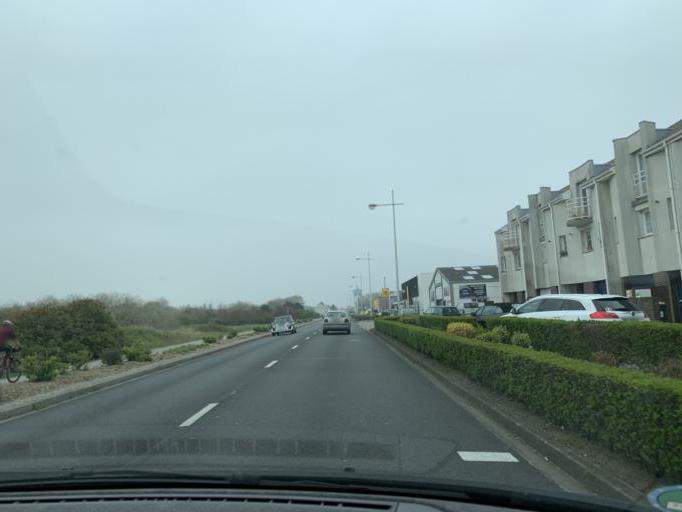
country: FR
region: Nord-Pas-de-Calais
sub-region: Departement du Pas-de-Calais
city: Coquelles
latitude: 50.9566
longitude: 1.8083
